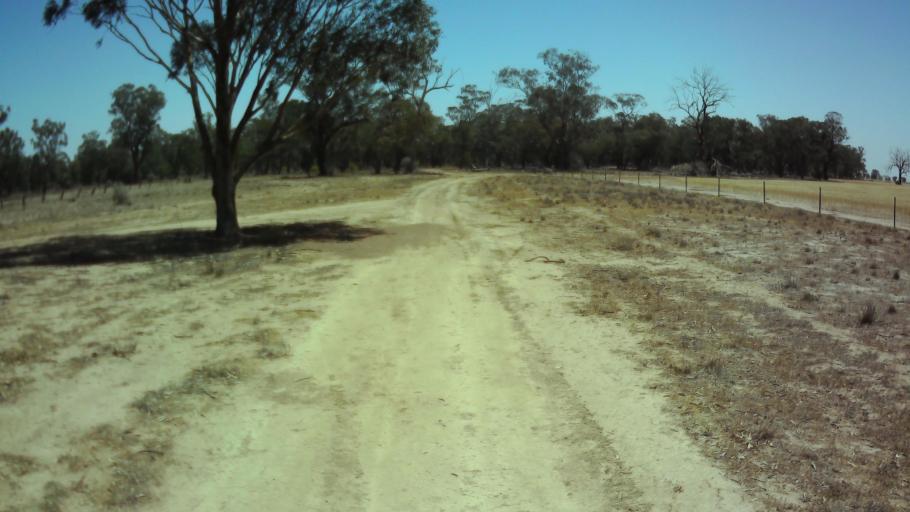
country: AU
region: New South Wales
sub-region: Weddin
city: Grenfell
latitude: -34.0697
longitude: 147.7923
